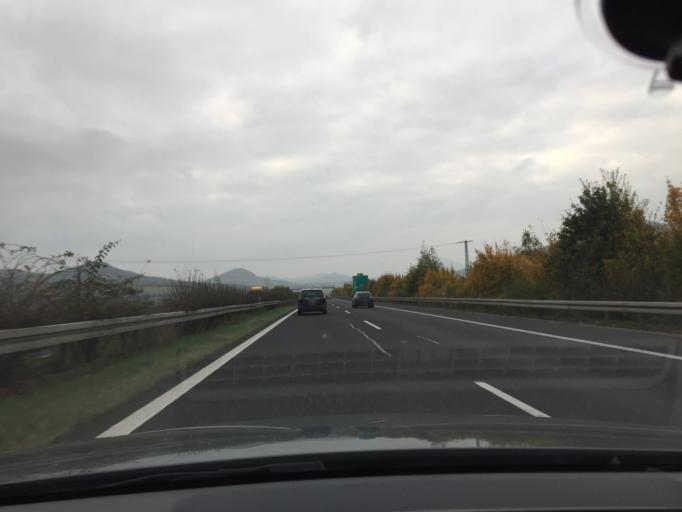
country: CZ
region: Ustecky
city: Lovosice
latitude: 50.5041
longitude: 14.0513
